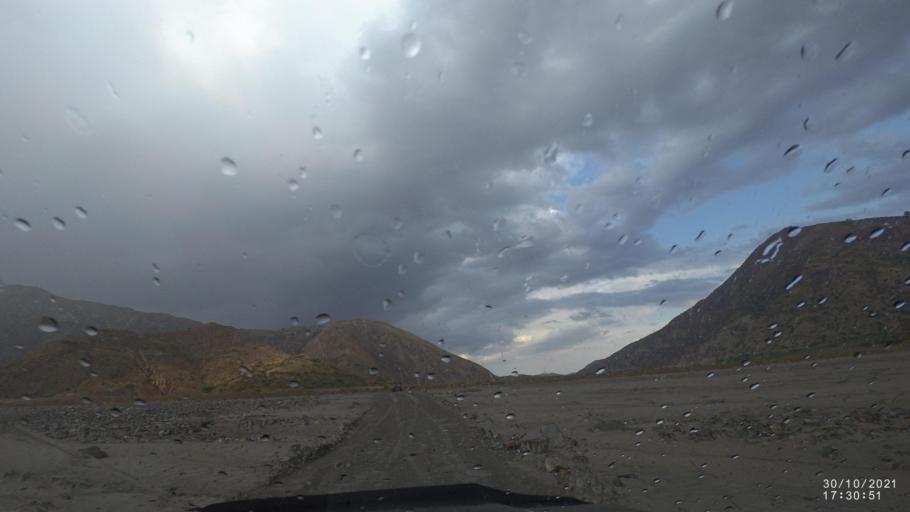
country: BO
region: Cochabamba
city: Sipe Sipe
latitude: -17.5236
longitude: -66.5957
